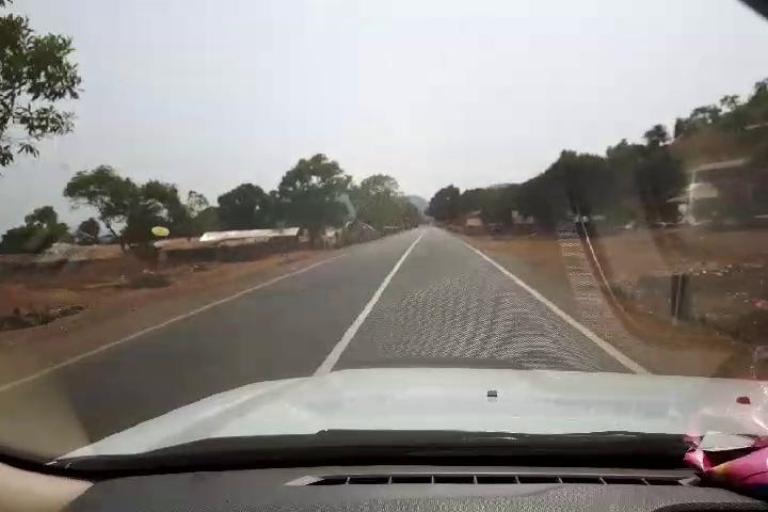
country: SL
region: Western Area
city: Waterloo
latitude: 8.2020
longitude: -13.1210
